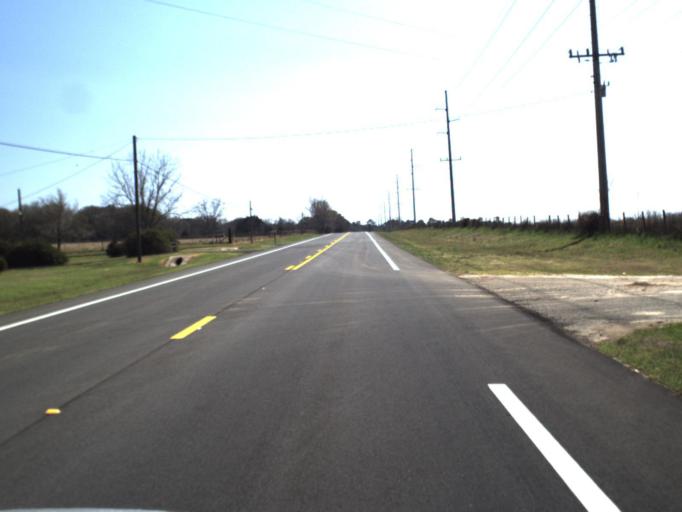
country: US
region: Florida
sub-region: Jackson County
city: Sneads
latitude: 30.7929
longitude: -85.0251
